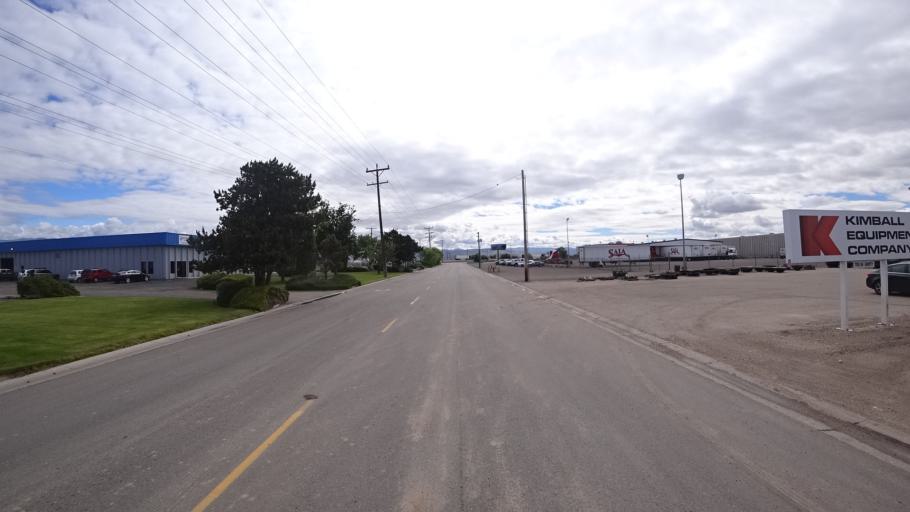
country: US
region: Idaho
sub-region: Ada County
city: Boise
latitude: 43.5604
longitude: -116.1904
